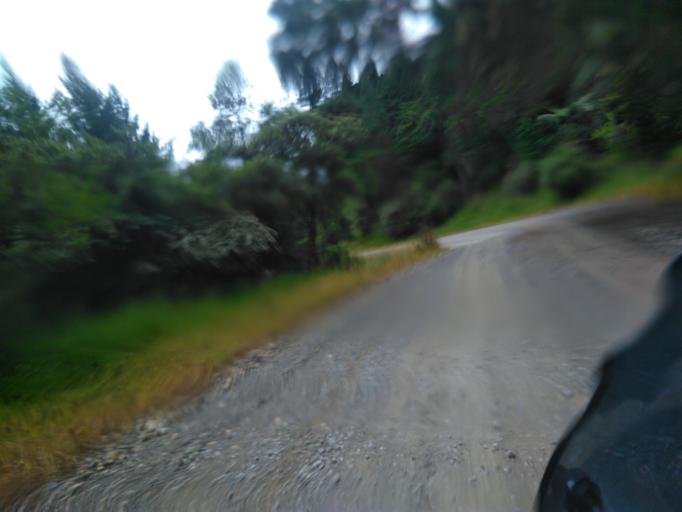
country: NZ
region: Gisborne
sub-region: Gisborne District
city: Gisborne
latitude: -38.0578
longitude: 178.1401
